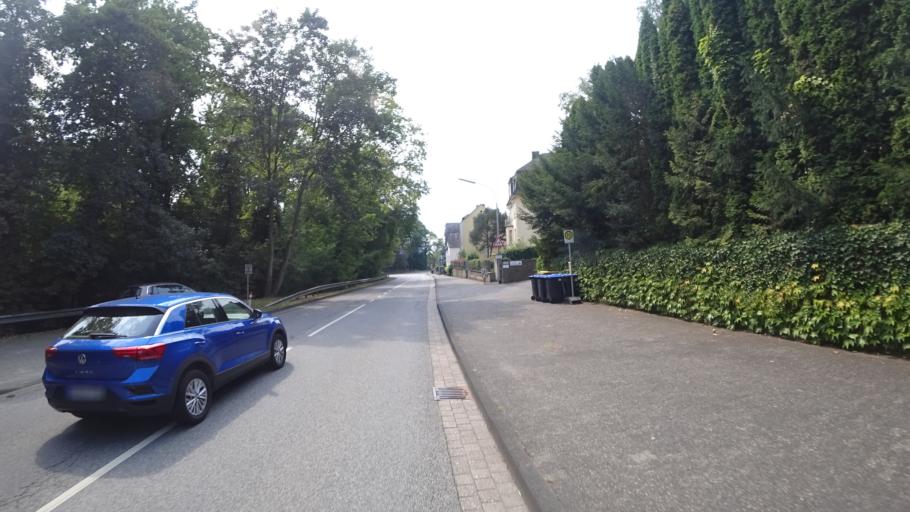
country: DE
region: Rheinland-Pfalz
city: Vallendar
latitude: 50.4044
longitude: 7.6269
